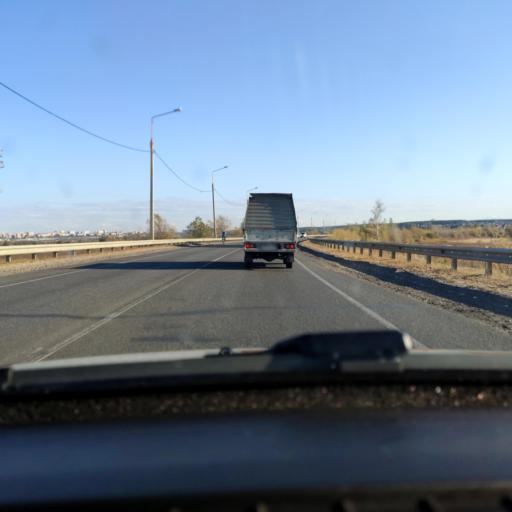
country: RU
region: Voronezj
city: Pridonskoy
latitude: 51.7214
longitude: 39.0688
